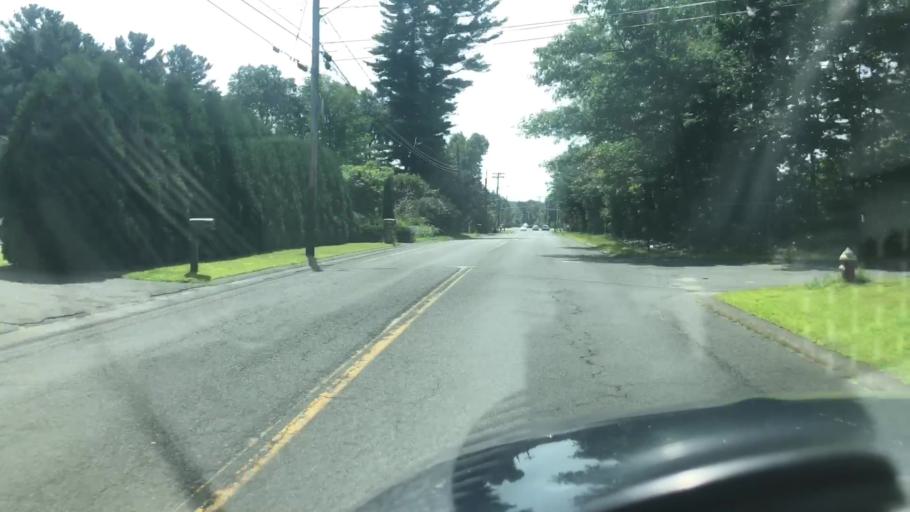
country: US
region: Massachusetts
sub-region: Hampshire County
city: Southampton
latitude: 42.1804
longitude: -72.6871
